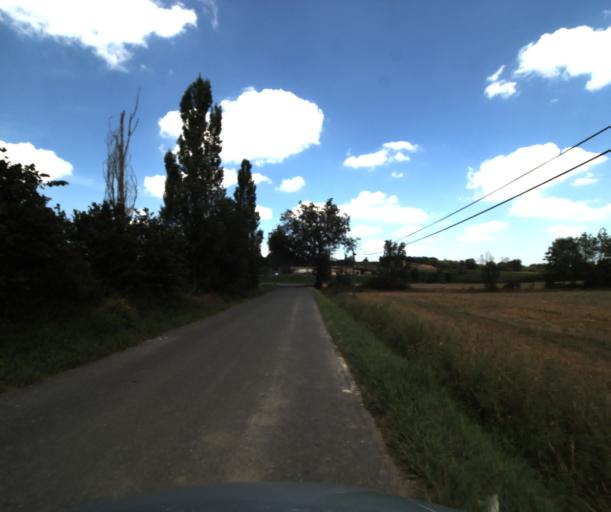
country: FR
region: Midi-Pyrenees
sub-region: Departement de la Haute-Garonne
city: Labastidette
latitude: 43.4595
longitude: 1.2181
